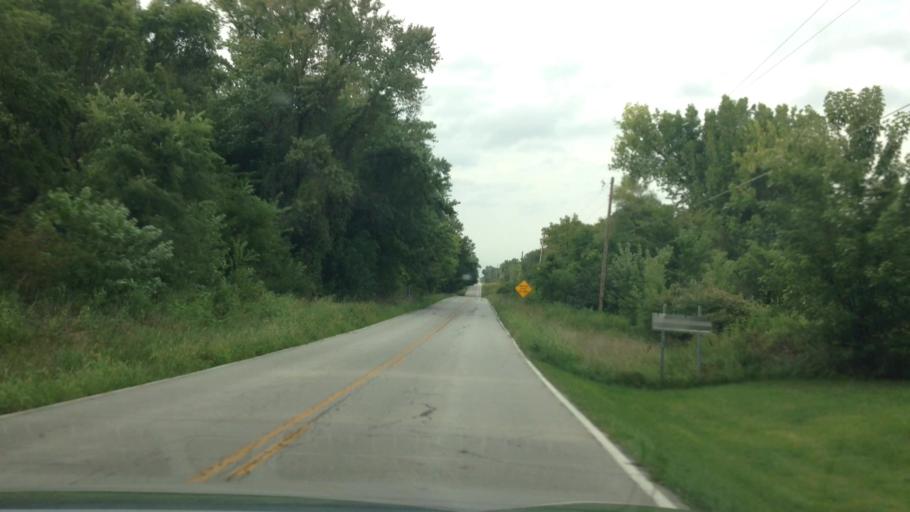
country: US
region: Missouri
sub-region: Clay County
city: Smithville
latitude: 39.3692
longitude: -94.6671
